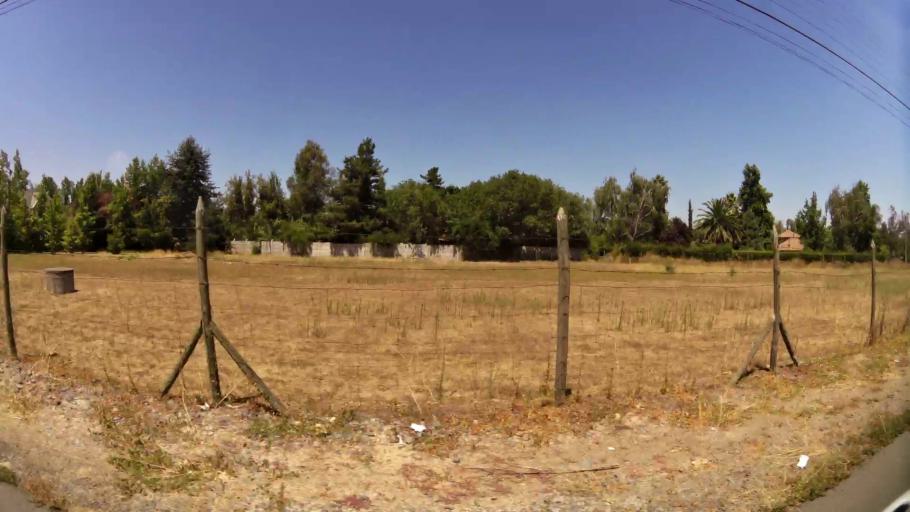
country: CL
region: Maule
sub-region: Provincia de Curico
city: Curico
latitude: -34.9936
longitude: -71.2097
